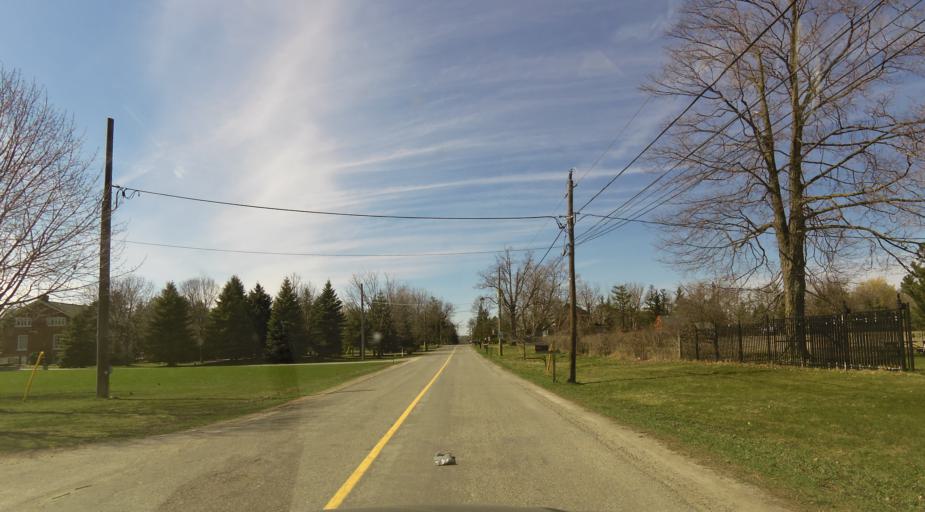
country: CA
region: Ontario
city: Brampton
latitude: 43.6277
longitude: -79.7528
